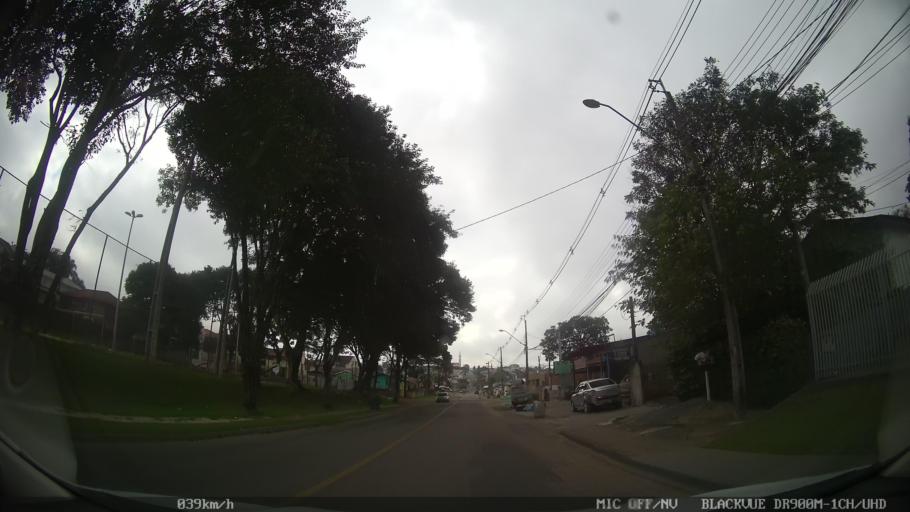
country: BR
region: Parana
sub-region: Curitiba
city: Curitiba
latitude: -25.3704
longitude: -49.2703
